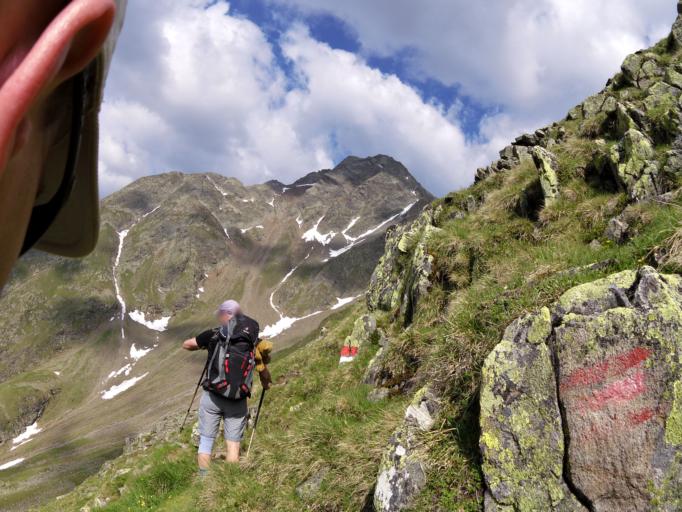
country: AT
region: Tyrol
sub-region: Politischer Bezirk Innsbruck Land
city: Gschnitz
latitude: 47.0323
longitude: 11.3001
